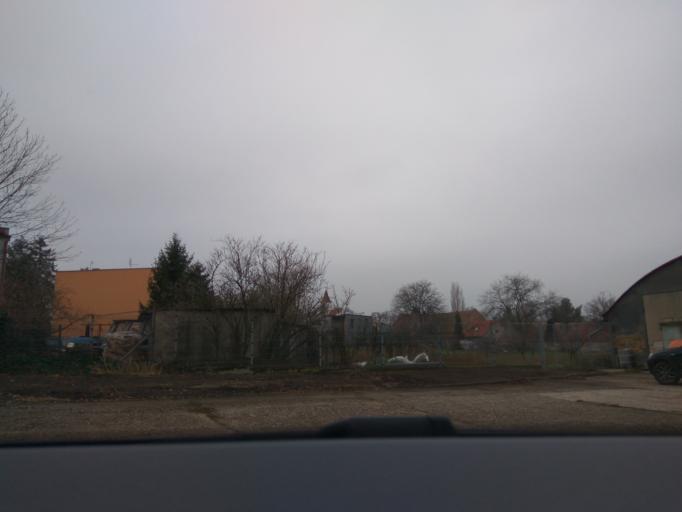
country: CZ
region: Central Bohemia
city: Hovorcovice
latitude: 50.1788
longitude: 14.5223
